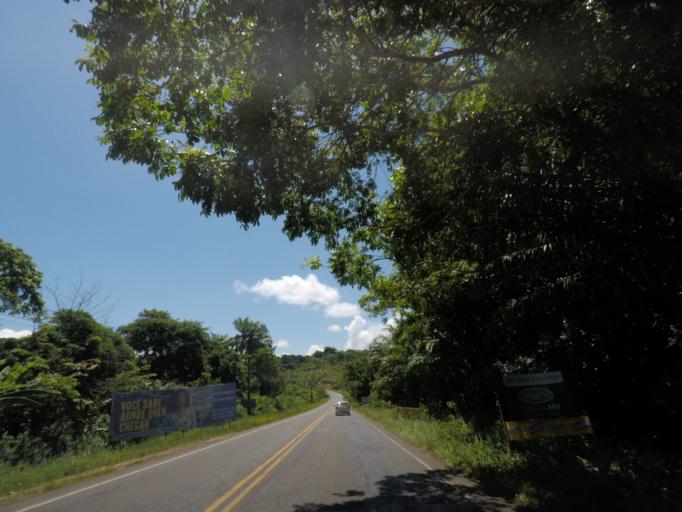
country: BR
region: Bahia
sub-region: Valenca
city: Valenca
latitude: -13.3290
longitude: -39.0510
